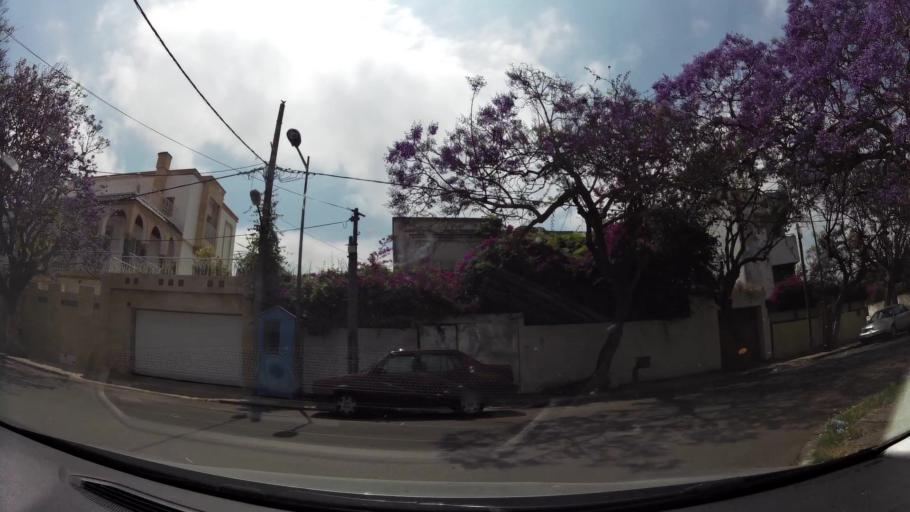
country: MA
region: Rabat-Sale-Zemmour-Zaer
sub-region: Rabat
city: Rabat
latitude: 34.0118
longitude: -6.8442
